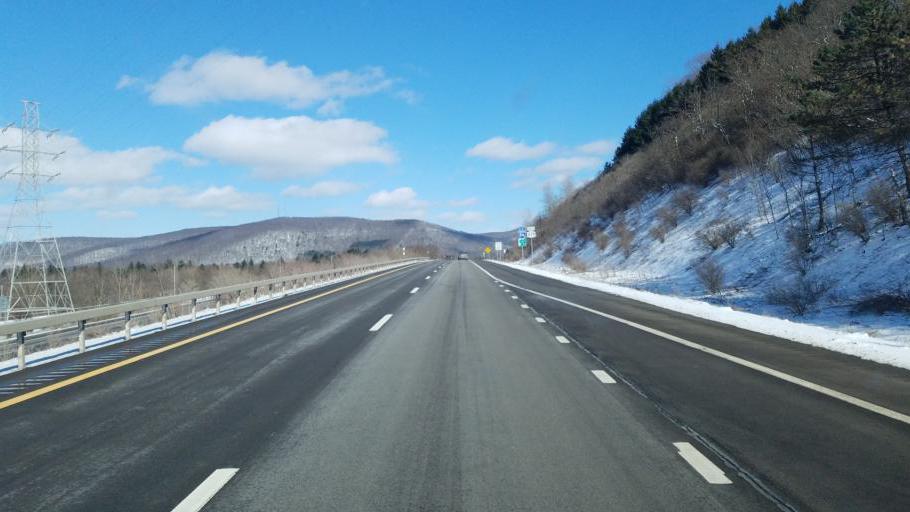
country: US
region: New York
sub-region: Cattaraugus County
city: Salamanca
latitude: 42.1502
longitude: -78.7052
